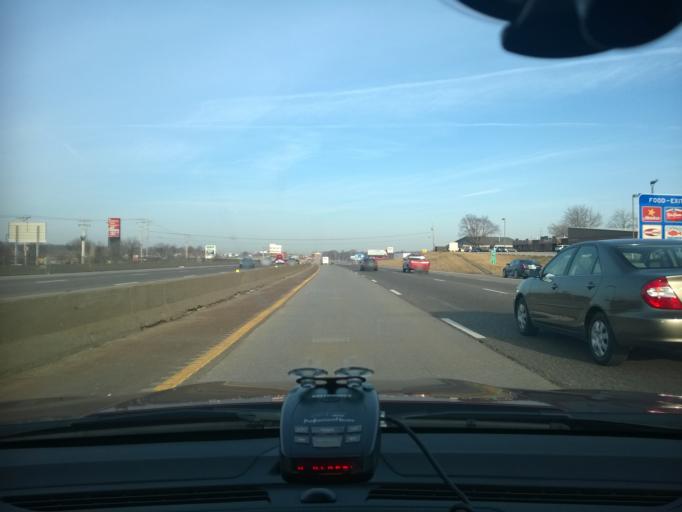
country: US
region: Missouri
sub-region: Saint Charles County
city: Saint Charles
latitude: 38.7837
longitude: -90.5232
